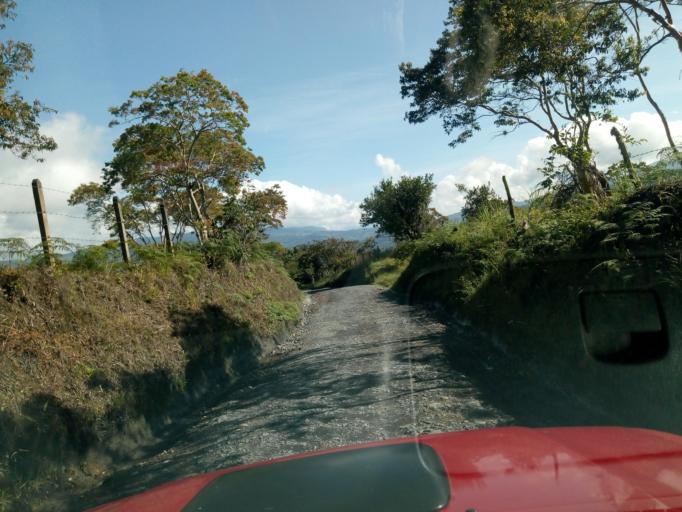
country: CO
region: Boyaca
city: Moniquira
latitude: 5.8878
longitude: -73.5366
